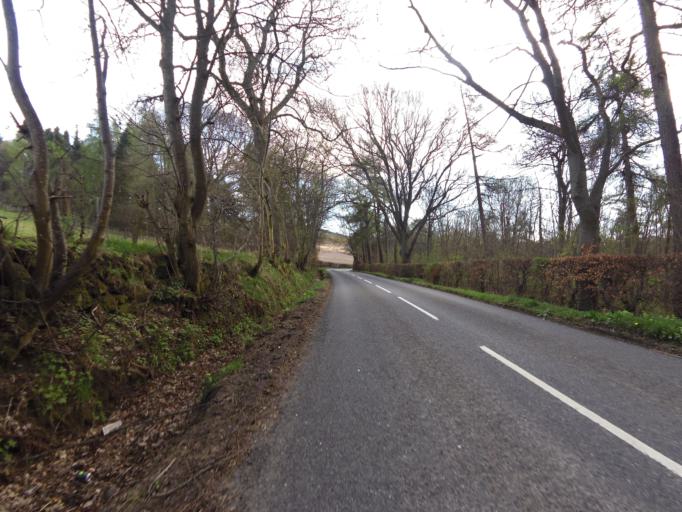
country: GB
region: Scotland
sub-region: Fife
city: Newburgh
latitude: 56.3286
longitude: -3.2294
